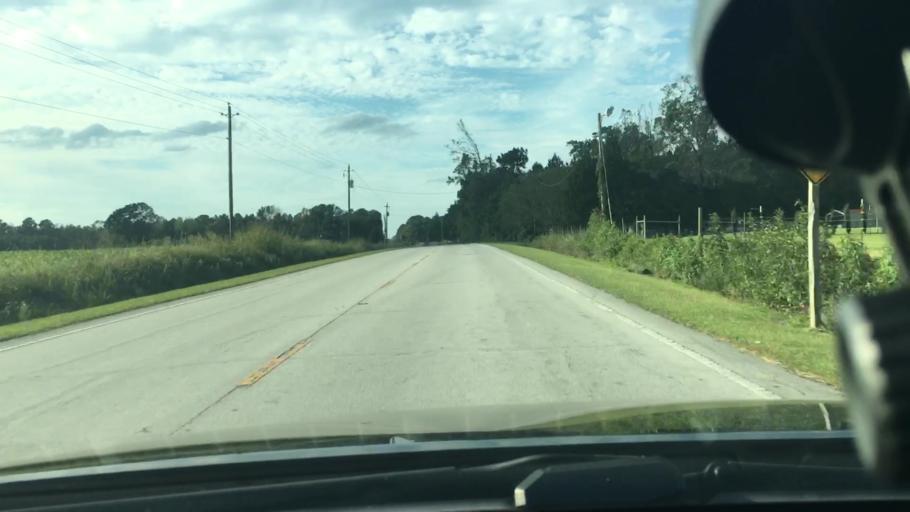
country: US
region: North Carolina
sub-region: Craven County
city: Vanceboro
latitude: 35.3390
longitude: -77.1760
